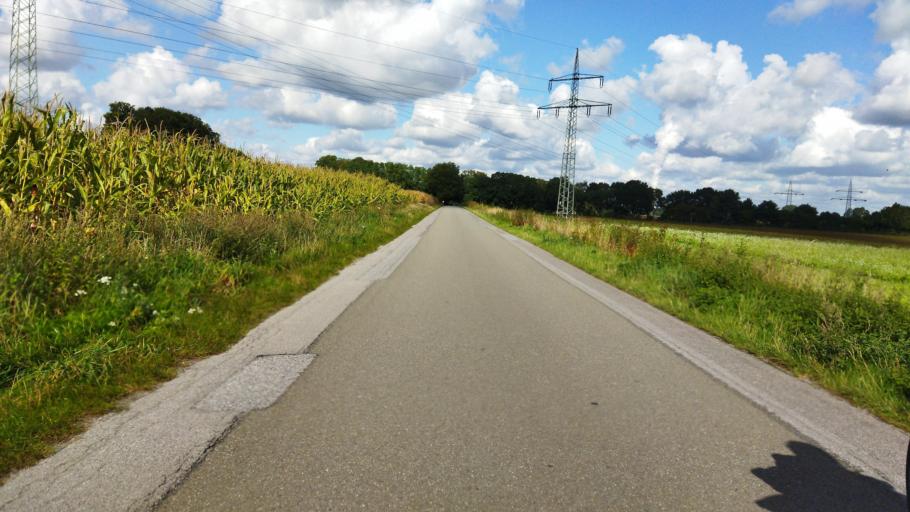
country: DE
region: Lower Saxony
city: Emsburen
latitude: 52.3897
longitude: 7.3264
